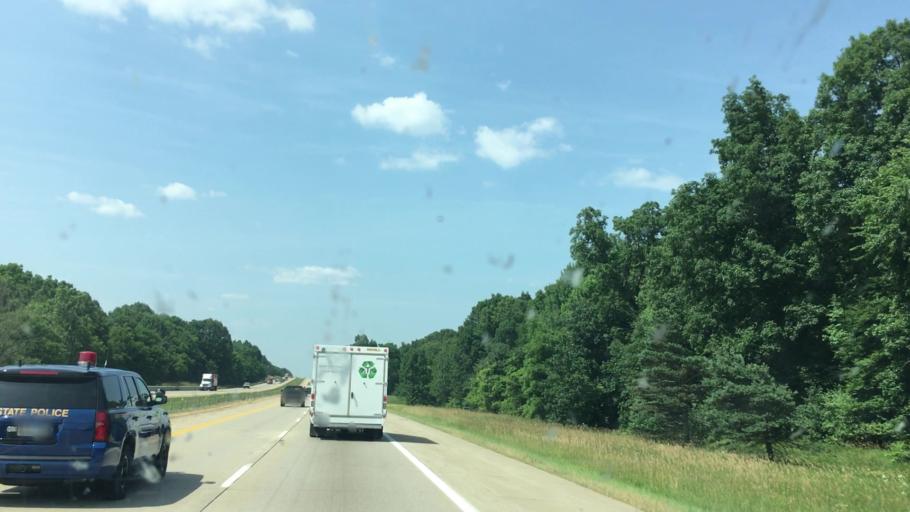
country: US
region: Michigan
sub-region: Allegan County
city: Plainwell
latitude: 42.4956
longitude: -85.6518
